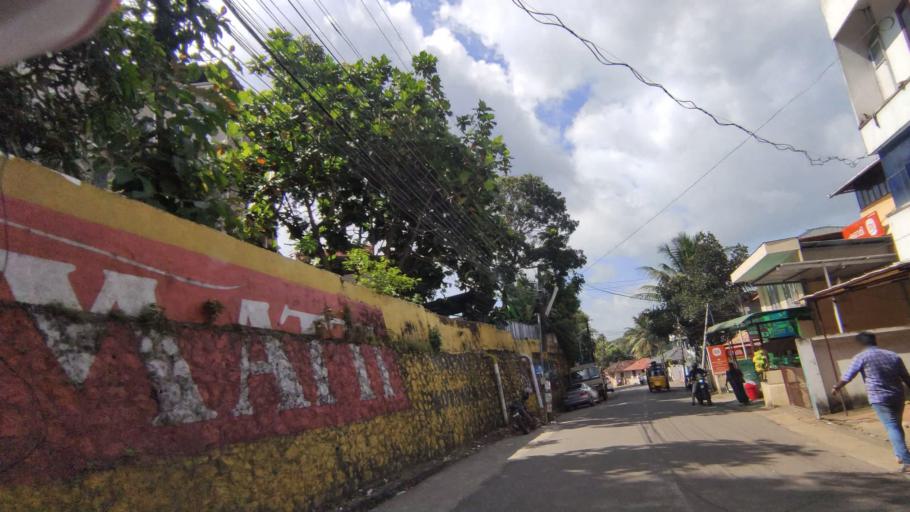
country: IN
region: Kerala
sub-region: Kottayam
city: Kottayam
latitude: 9.5876
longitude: 76.5290
